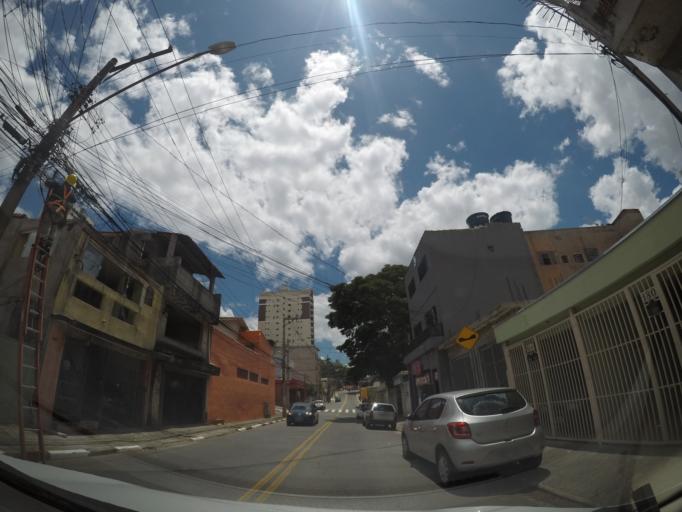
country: BR
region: Sao Paulo
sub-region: Guarulhos
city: Guarulhos
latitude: -23.4613
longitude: -46.5453
